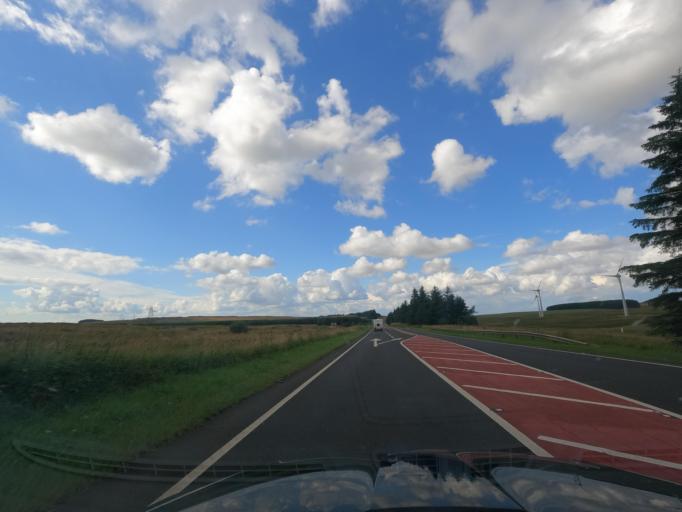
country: GB
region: Scotland
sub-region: East Lothian
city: Pencaitland
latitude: 55.8143
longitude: -2.8445
